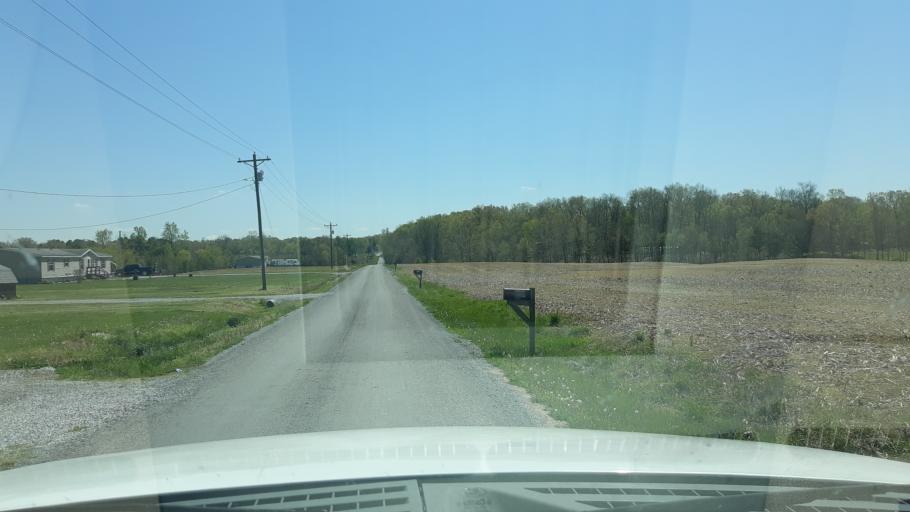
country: US
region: Illinois
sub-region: Saline County
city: Harrisburg
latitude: 37.8773
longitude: -88.6421
